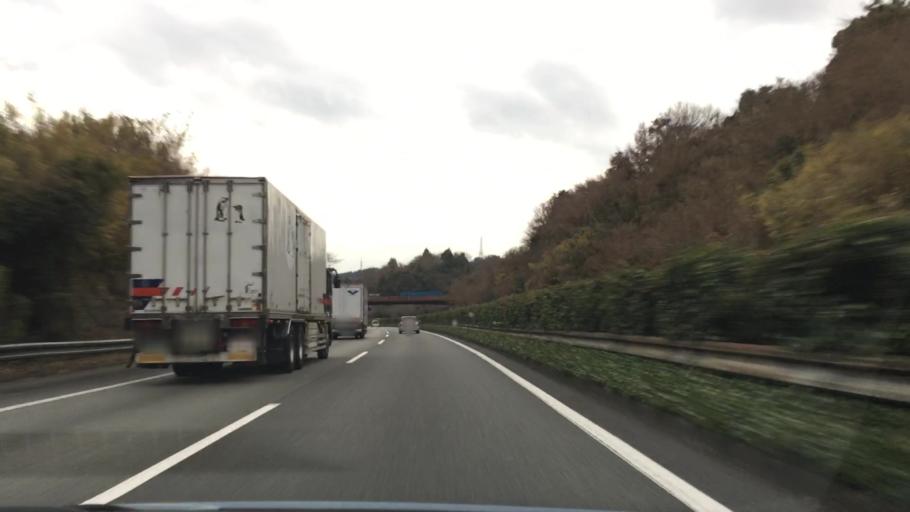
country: JP
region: Shizuoka
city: Fujinomiya
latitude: 35.1469
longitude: 138.6143
